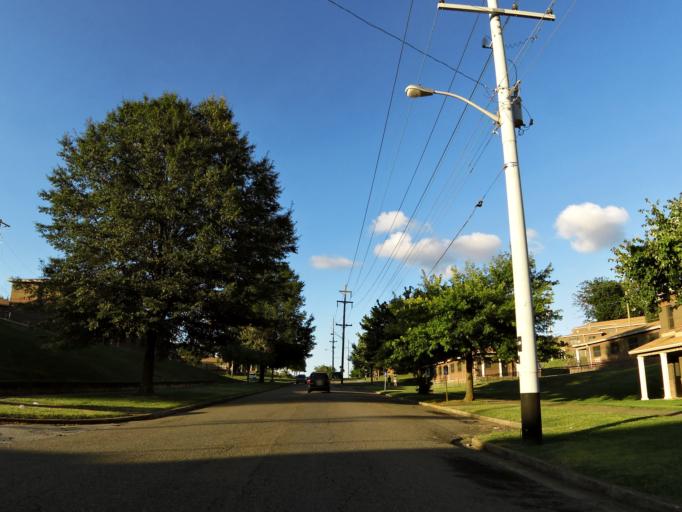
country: US
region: Tennessee
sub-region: Knox County
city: Knoxville
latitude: 35.9769
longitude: -83.9454
